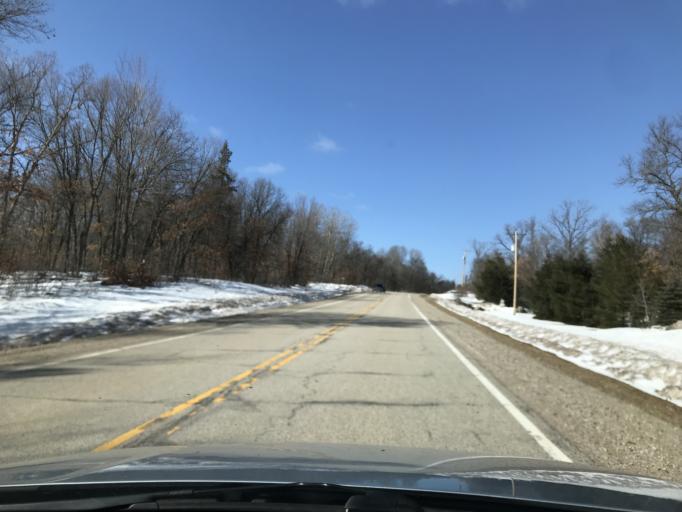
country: US
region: Wisconsin
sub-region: Marinette County
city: Niagara
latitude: 45.3383
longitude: -88.1008
